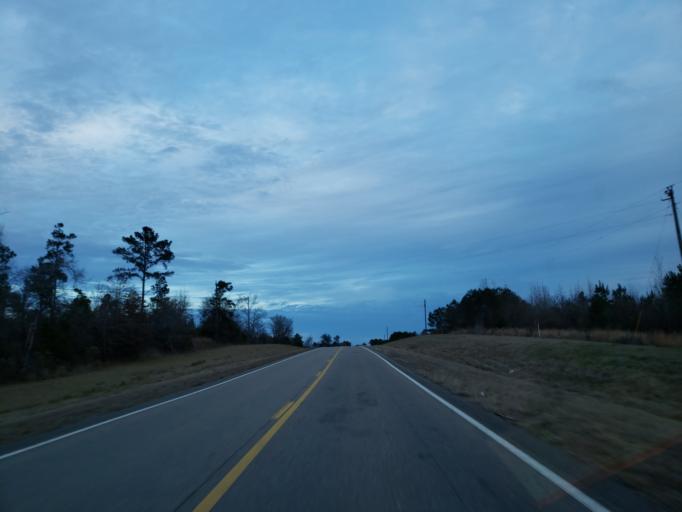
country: US
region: Mississippi
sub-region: Kemper County
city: De Kalb
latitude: 32.8308
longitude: -88.3734
